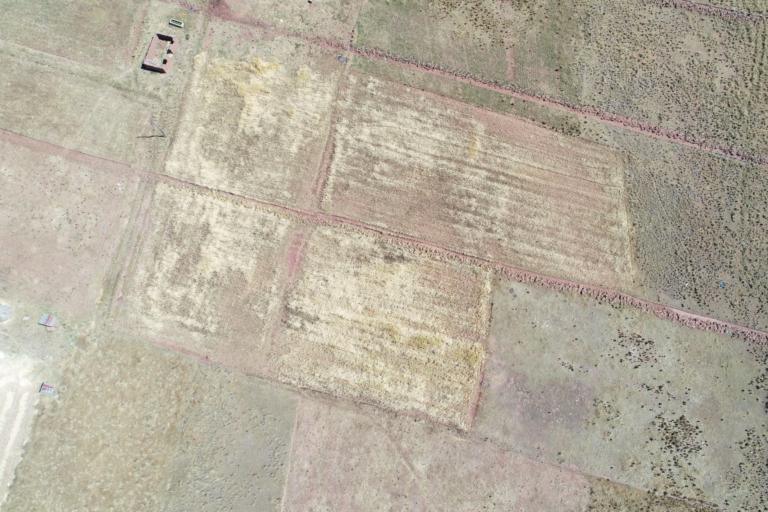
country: BO
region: La Paz
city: Tiahuanaco
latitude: -16.5929
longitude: -68.7738
